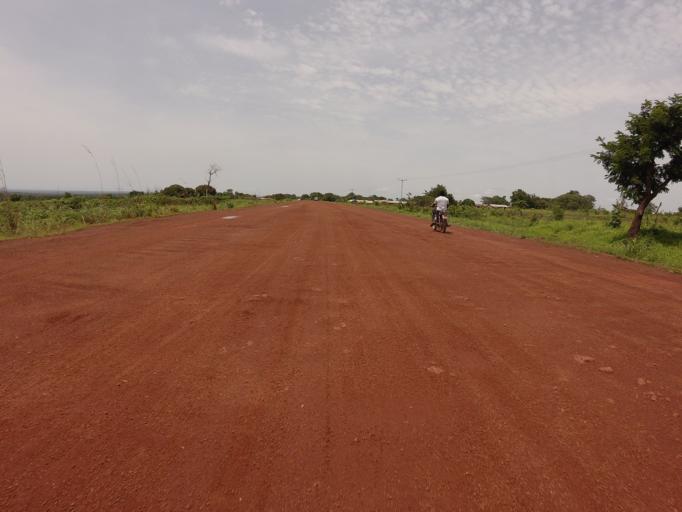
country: GH
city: Kpandae
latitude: 8.7390
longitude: 0.0828
